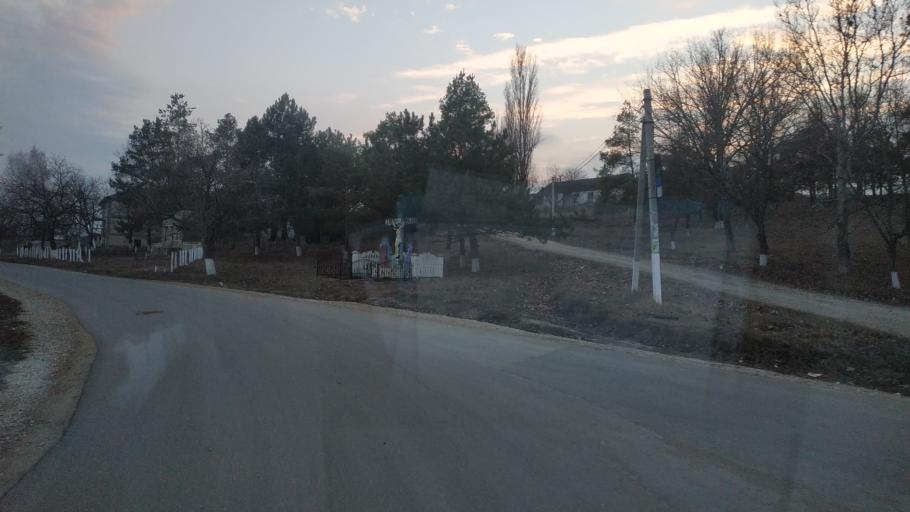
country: MD
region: Hincesti
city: Dancu
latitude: 46.6607
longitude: 28.3064
